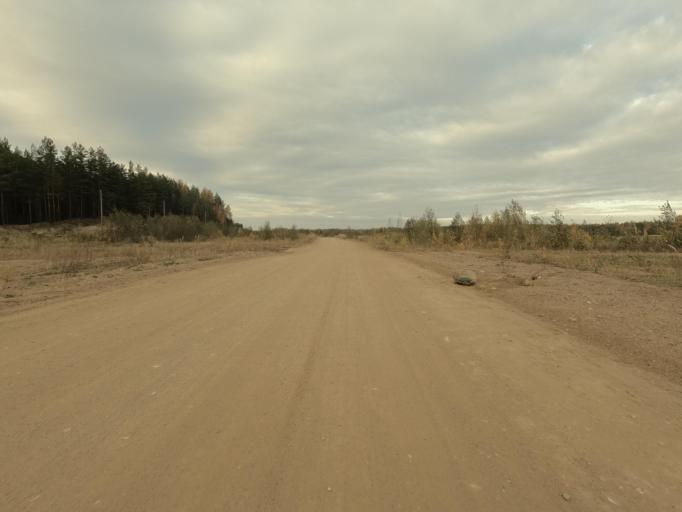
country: RU
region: Leningrad
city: Priladozhskiy
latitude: 59.7031
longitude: 31.3632
